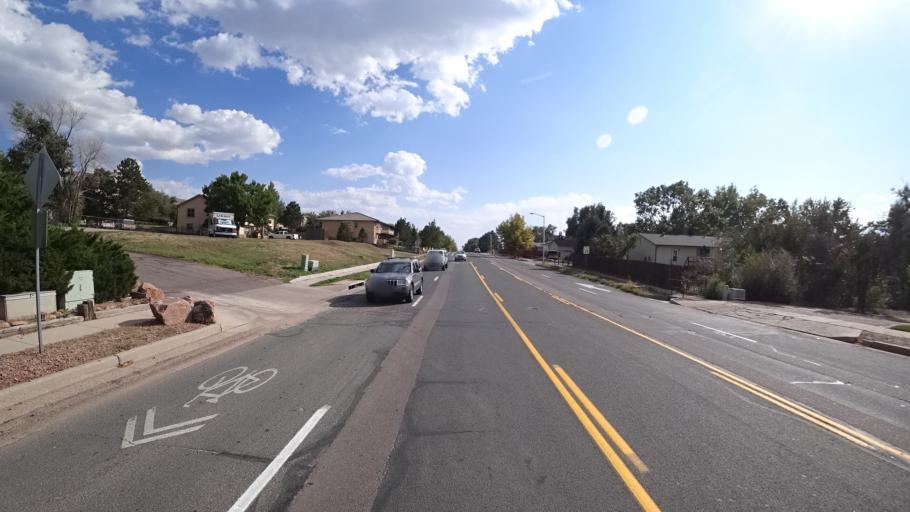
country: US
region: Colorado
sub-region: El Paso County
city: Cimarron Hills
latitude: 38.8961
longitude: -104.7385
